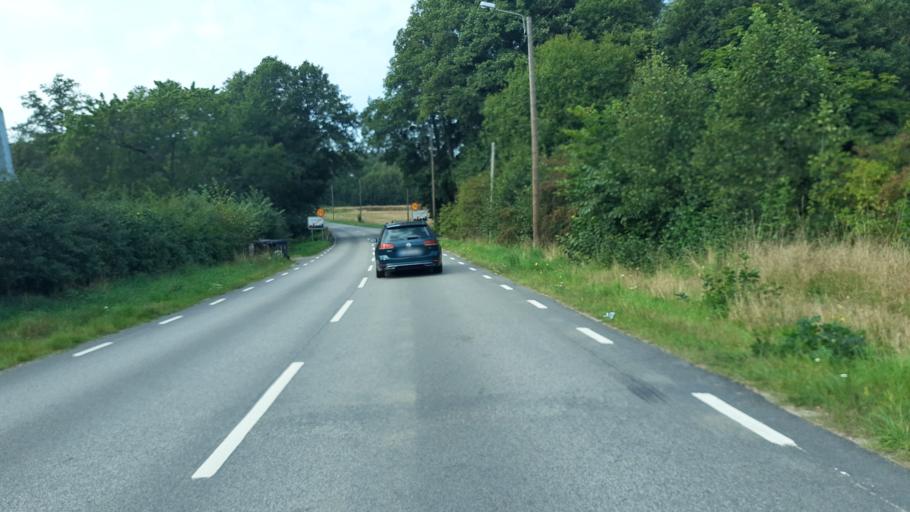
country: SE
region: Blekinge
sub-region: Karlskrona Kommun
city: Nattraby
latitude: 56.2207
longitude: 15.4116
